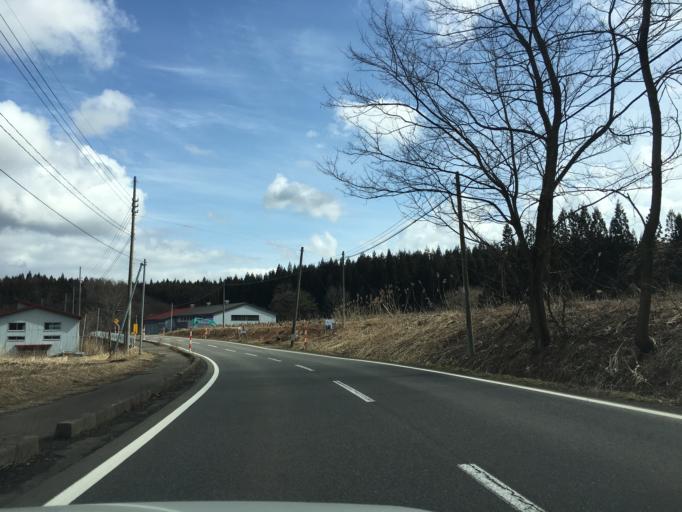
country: JP
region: Akita
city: Odate
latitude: 40.2011
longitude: 140.5466
